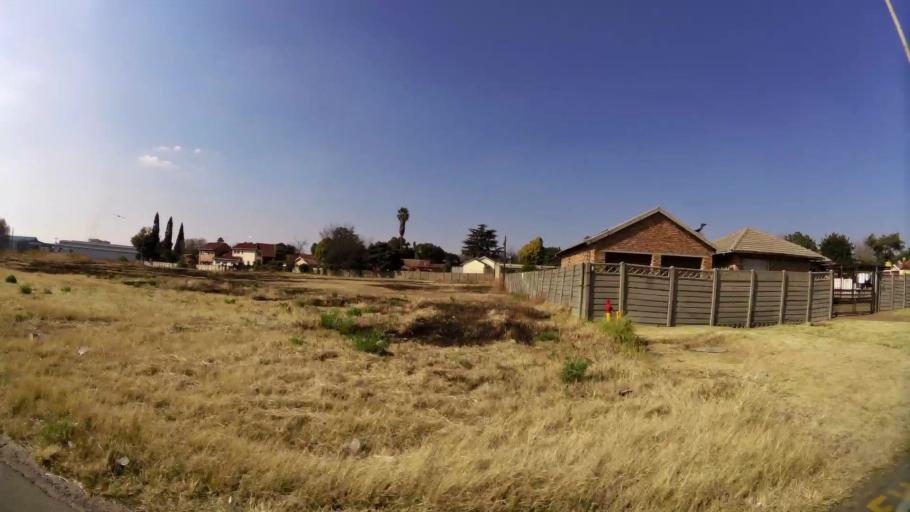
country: ZA
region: Gauteng
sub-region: City of Johannesburg Metropolitan Municipality
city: Modderfontein
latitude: -26.1197
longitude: 28.2227
